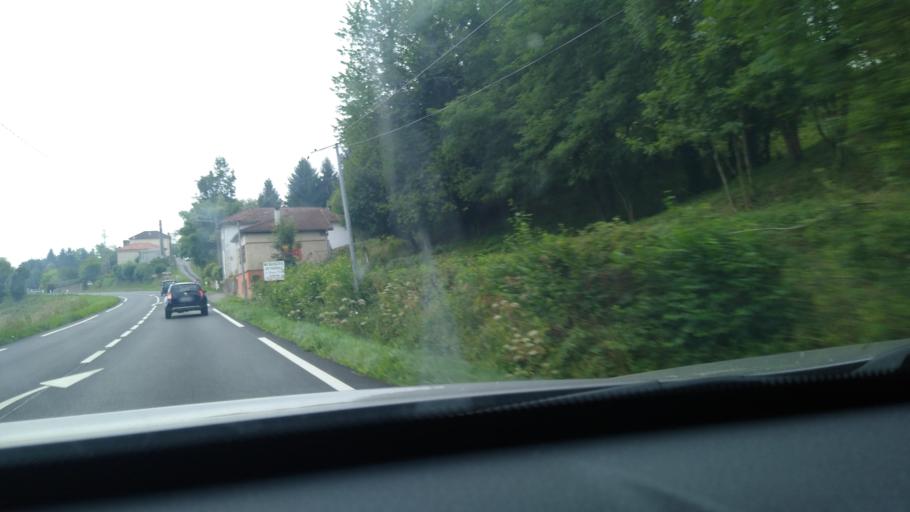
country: FR
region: Midi-Pyrenees
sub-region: Departement de la Haute-Garonne
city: Salies-du-Salat
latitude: 43.0699
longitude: 0.9667
